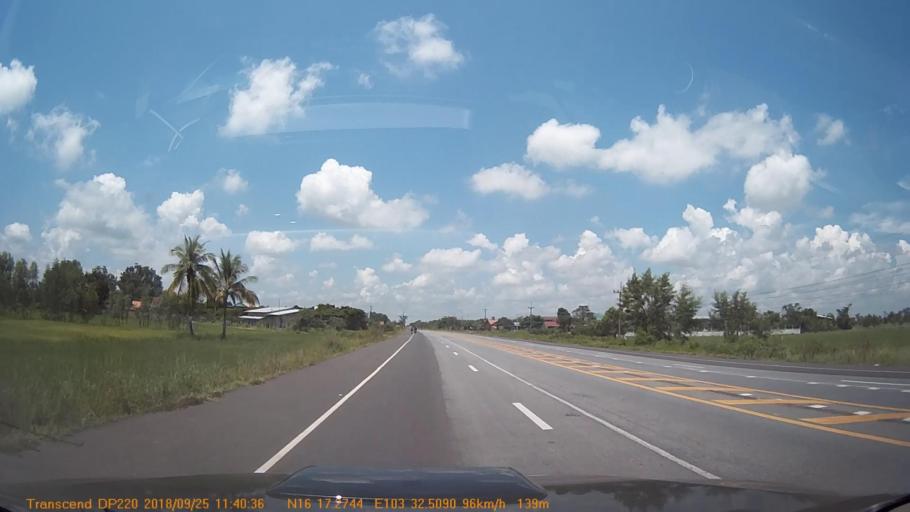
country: TH
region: Kalasin
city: Kamalasai
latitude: 16.2878
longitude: 103.5421
